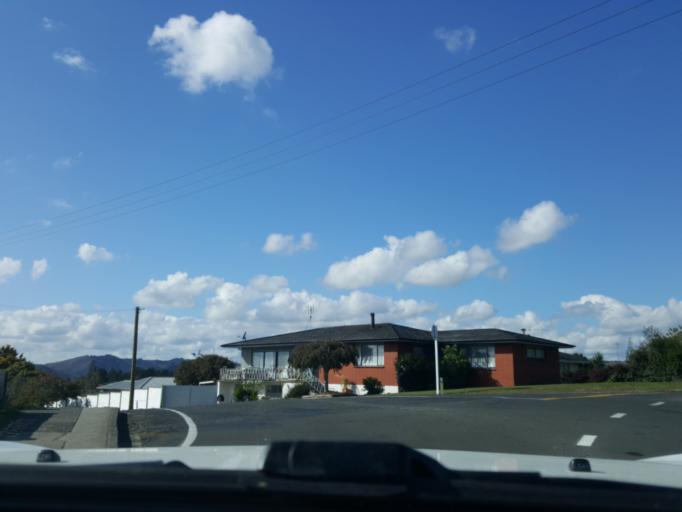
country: NZ
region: Waikato
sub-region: Waikato District
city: Ngaruawahia
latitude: -37.5472
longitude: 175.1679
